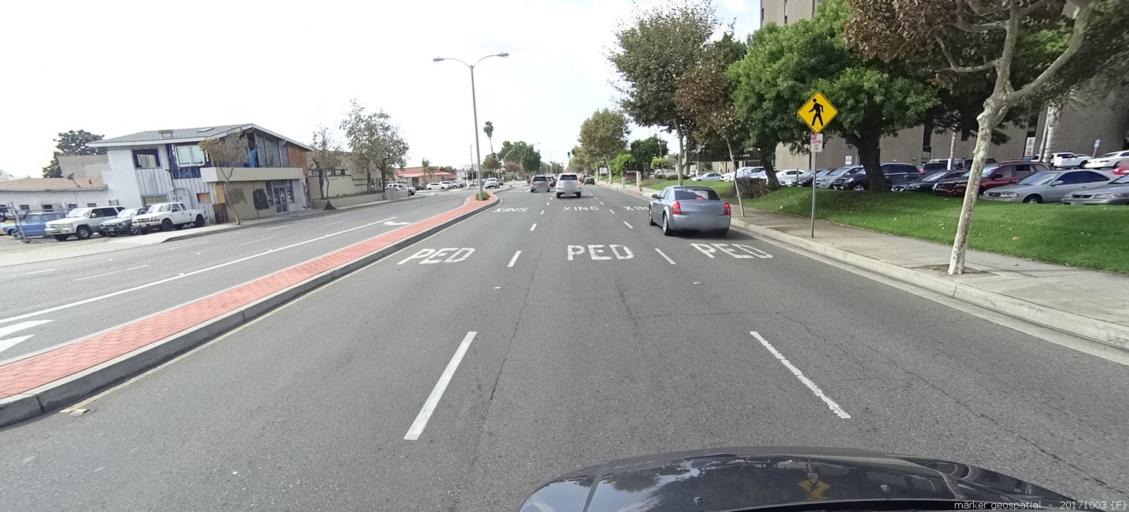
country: US
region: California
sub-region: Orange County
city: Garden Grove
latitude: 33.7745
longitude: -117.9119
